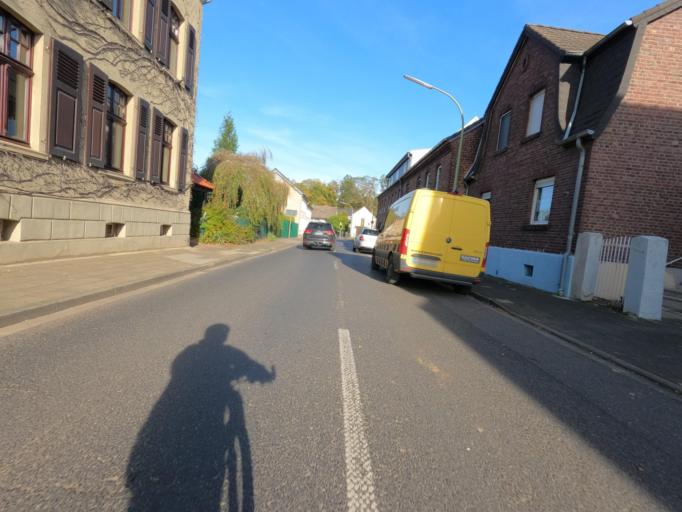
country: DE
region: North Rhine-Westphalia
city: Erkelenz
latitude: 51.0332
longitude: 6.3247
